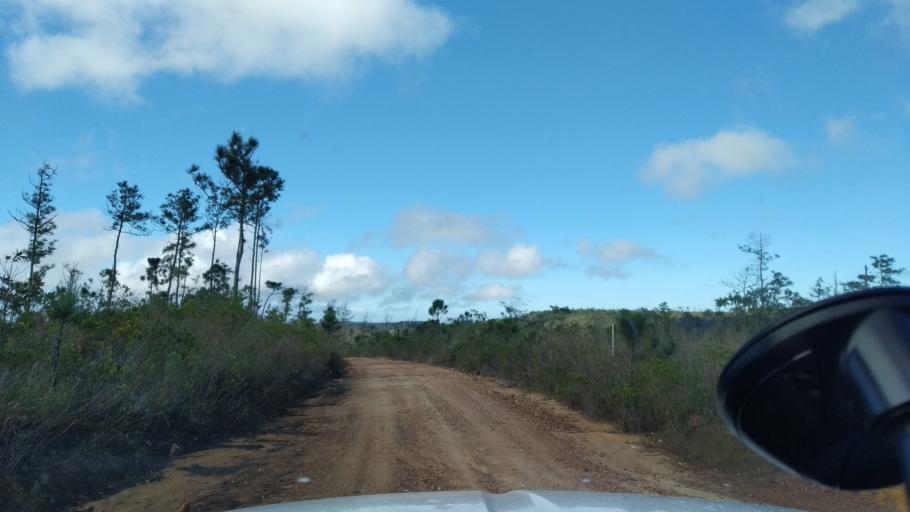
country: BZ
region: Cayo
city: Belmopan
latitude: 16.9966
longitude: -88.8342
